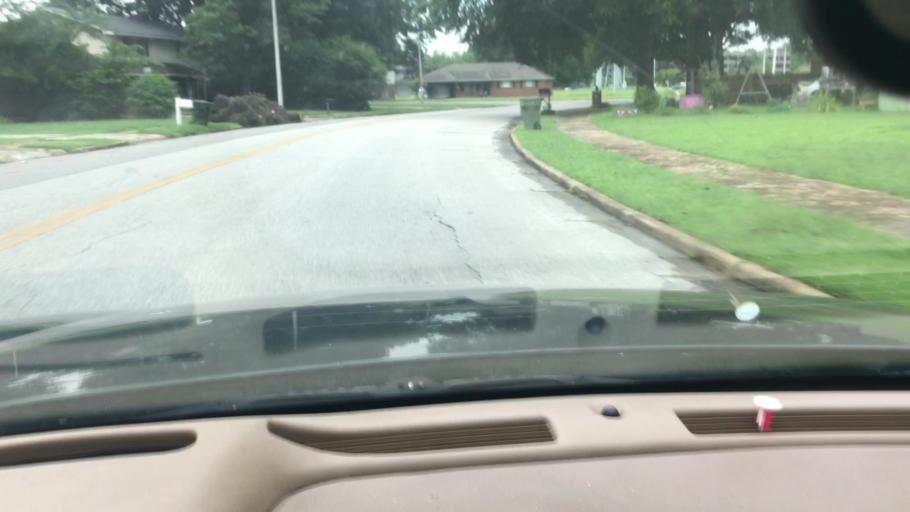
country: US
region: Tennessee
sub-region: Shelby County
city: Germantown
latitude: 35.0732
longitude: -89.8992
